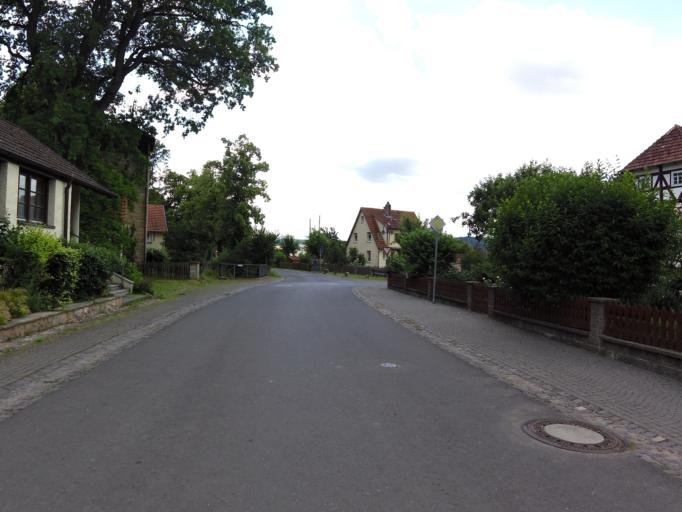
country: DE
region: Thuringia
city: Lauchroden
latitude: 51.0051
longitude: 10.1605
